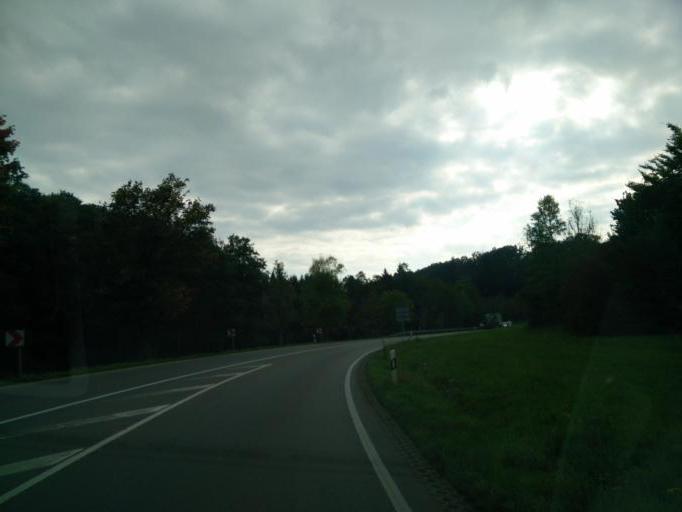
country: DE
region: Baden-Wuerttemberg
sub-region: Tuebingen Region
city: Bad Wurzach
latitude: 47.8994
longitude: 9.8976
